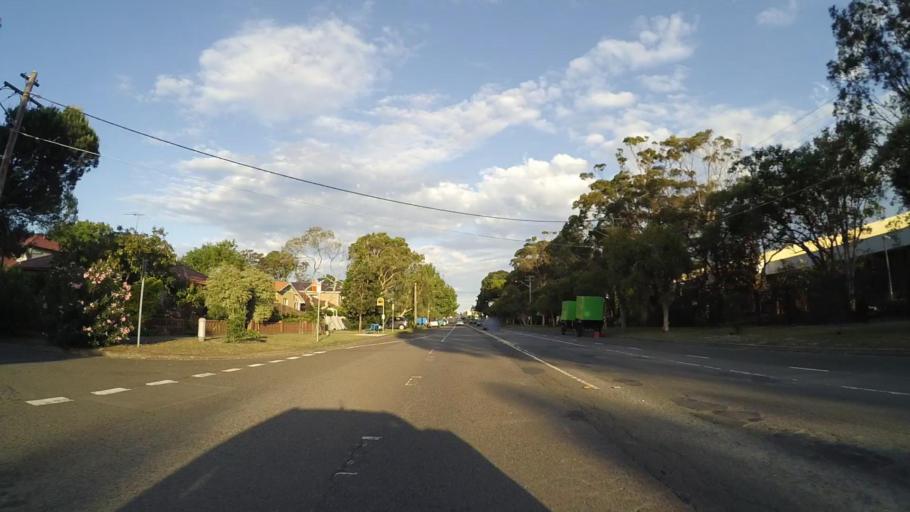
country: AU
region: New South Wales
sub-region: Randwick
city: Daceyville
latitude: -33.9398
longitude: 151.2261
